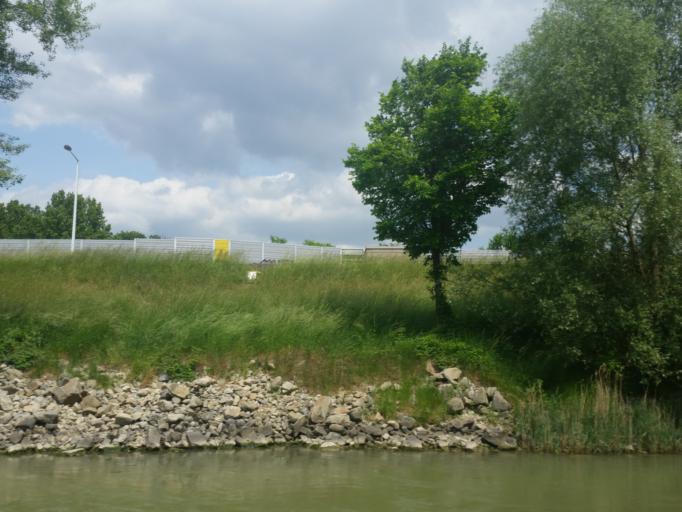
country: AT
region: Vienna
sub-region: Wien Stadt
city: Vienna
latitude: 48.1870
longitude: 16.4300
